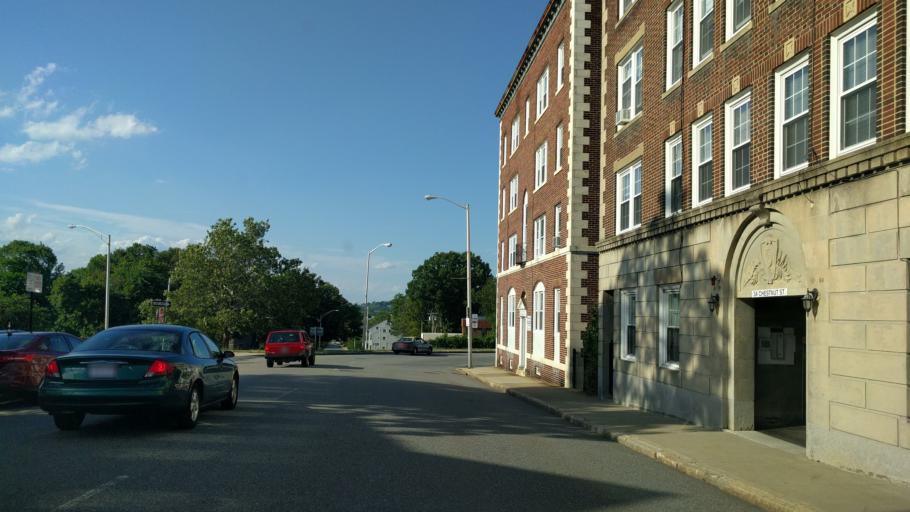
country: US
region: Massachusetts
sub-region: Worcester County
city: Worcester
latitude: 42.2671
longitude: -71.8036
